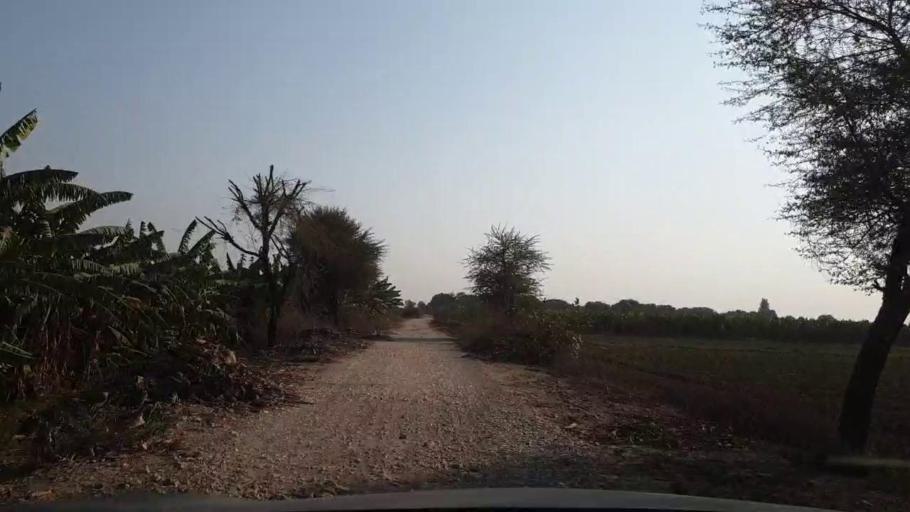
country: PK
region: Sindh
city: Tando Allahyar
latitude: 25.5799
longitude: 68.7642
